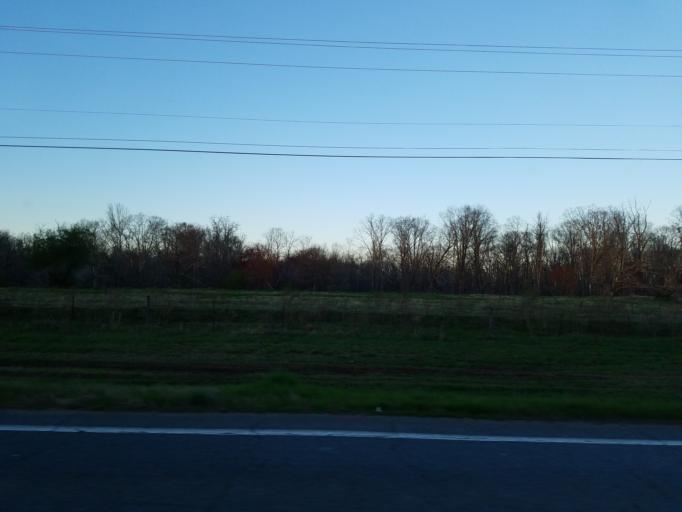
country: US
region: Georgia
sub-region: Hall County
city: Oakwood
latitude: 34.3062
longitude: -83.9831
